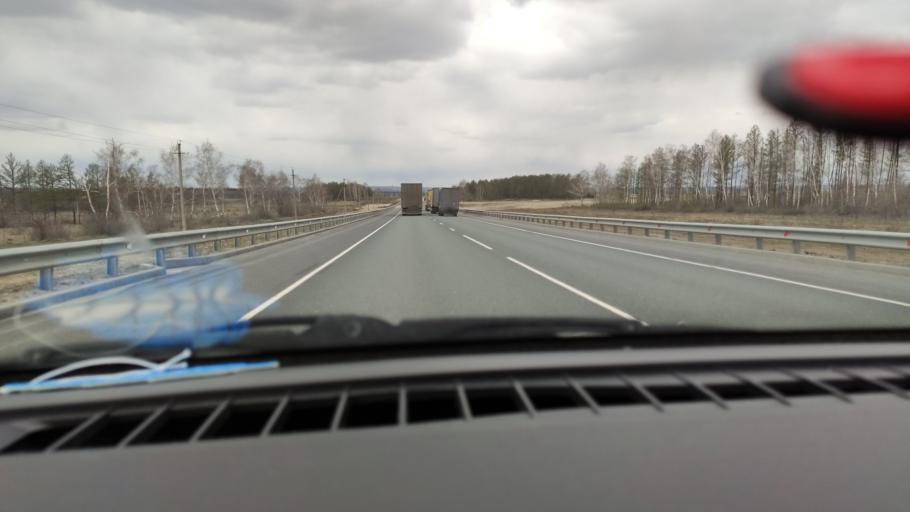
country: RU
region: Saratov
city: Shikhany
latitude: 52.1607
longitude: 47.0962
